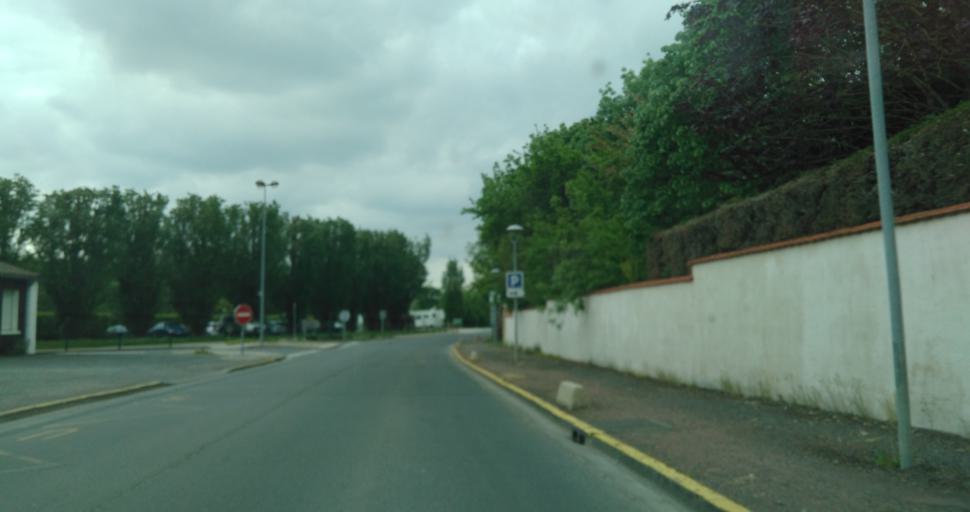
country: FR
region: Poitou-Charentes
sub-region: Departement des Deux-Sevres
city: Coulon
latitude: 46.3221
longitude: -0.5889
